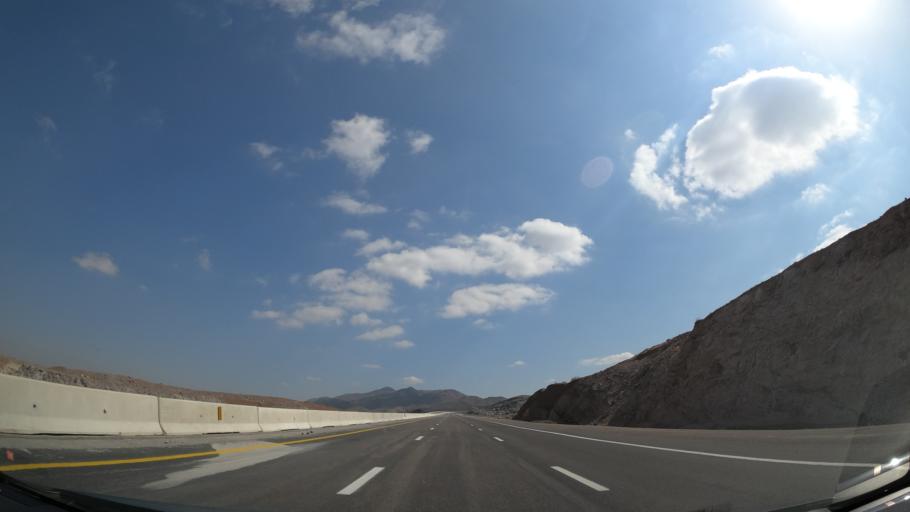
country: IR
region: Alborz
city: Nazarabad
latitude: 35.6988
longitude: 50.6243
